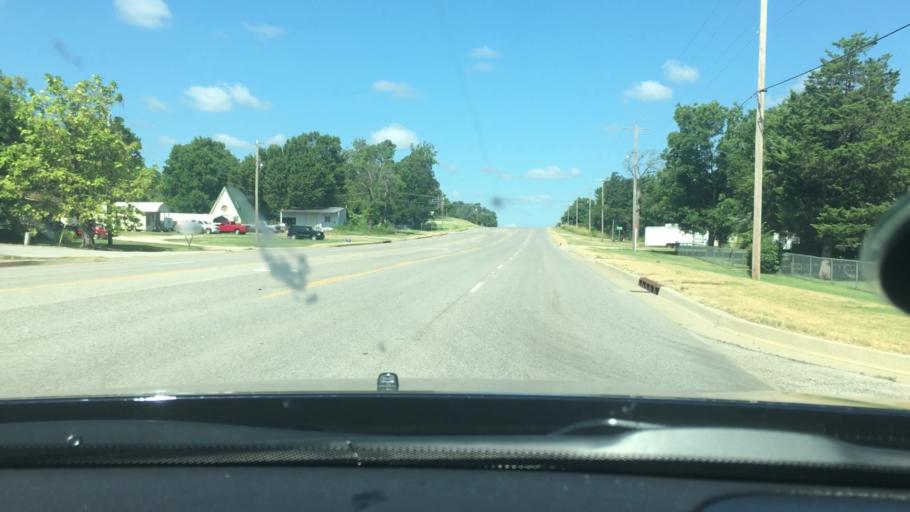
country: US
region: Oklahoma
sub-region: Marshall County
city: Oakland
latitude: 34.1000
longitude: -96.7941
